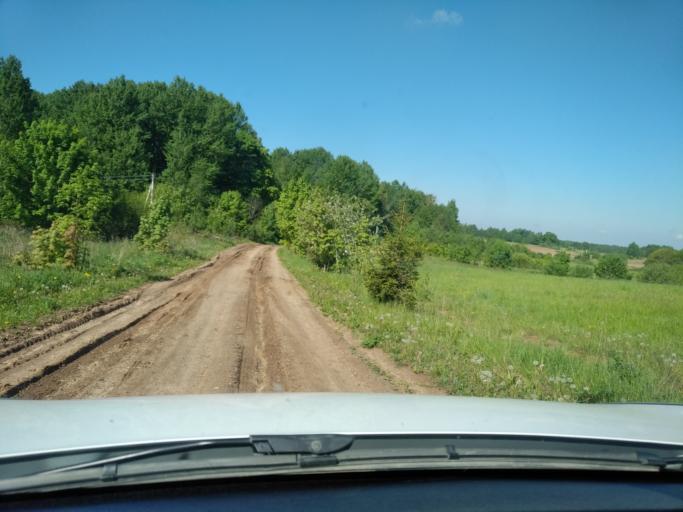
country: LT
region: Panevezys
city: Rokiskis
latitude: 55.7485
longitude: 25.6097
